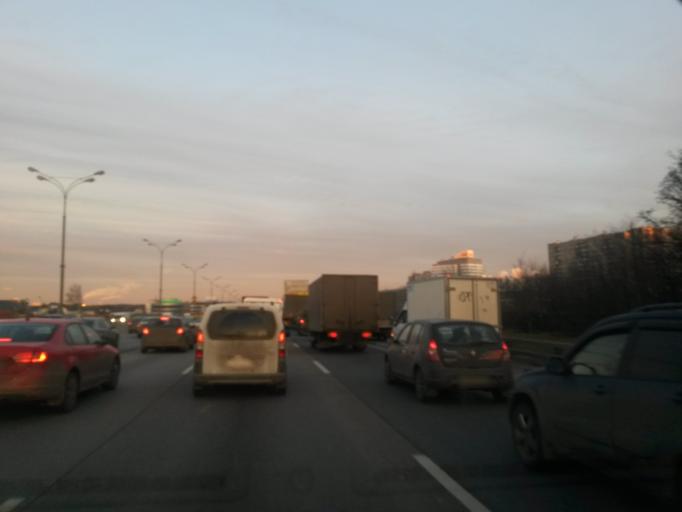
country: RU
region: Moskovskaya
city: Mosrentgen
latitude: 55.6254
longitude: 37.4756
